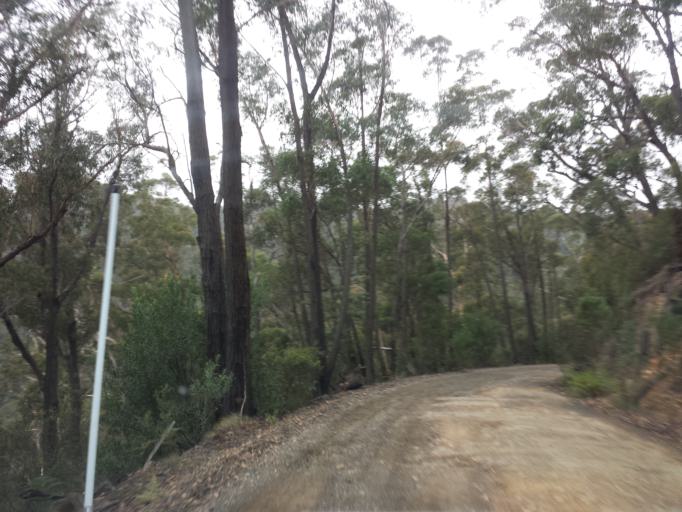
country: AU
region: Victoria
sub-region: Latrobe
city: Traralgon
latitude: -37.9539
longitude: 146.4460
